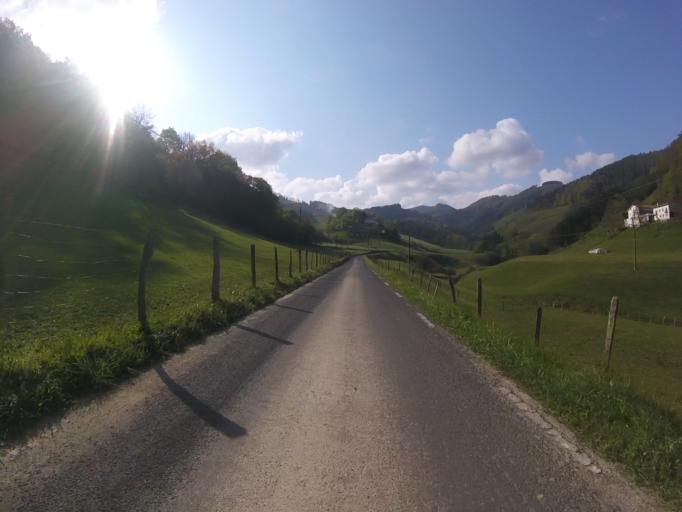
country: ES
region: Basque Country
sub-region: Provincia de Guipuzcoa
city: Azkoitia
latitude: 43.2331
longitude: -2.3223
